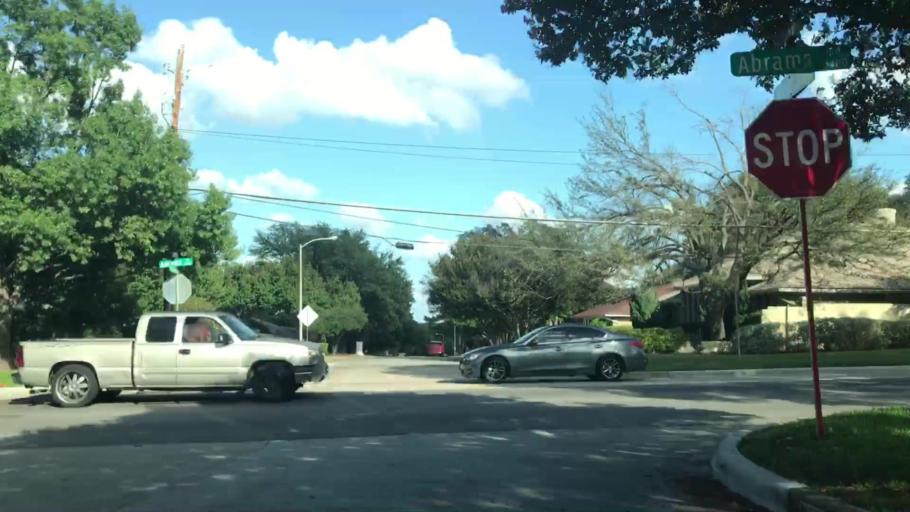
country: US
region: Texas
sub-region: Dallas County
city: Highland Park
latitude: 32.8293
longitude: -96.7531
